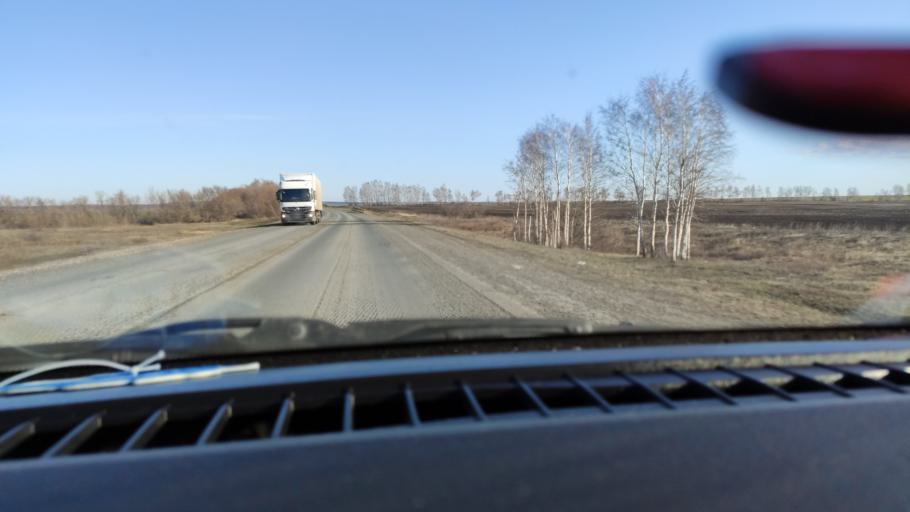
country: RU
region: Saratov
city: Dukhovnitskoye
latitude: 52.7162
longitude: 48.2668
